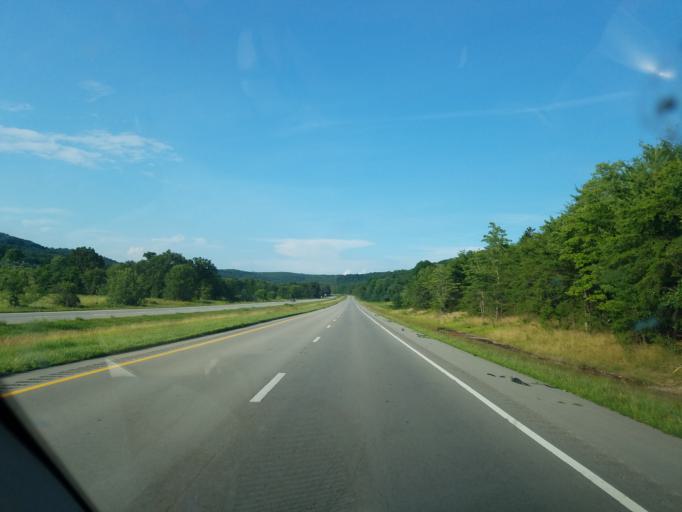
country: US
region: Ohio
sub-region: Adams County
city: Peebles
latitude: 38.9883
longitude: -83.3150
